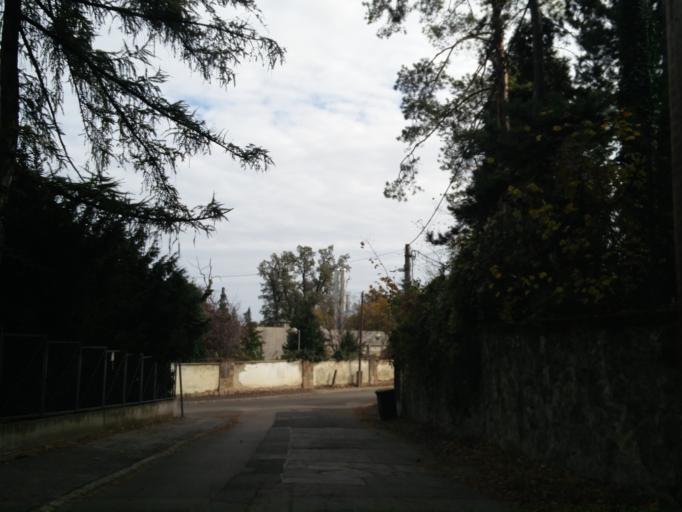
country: HU
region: Budapest
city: Budapest XII. keruelet
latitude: 47.5038
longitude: 18.9775
